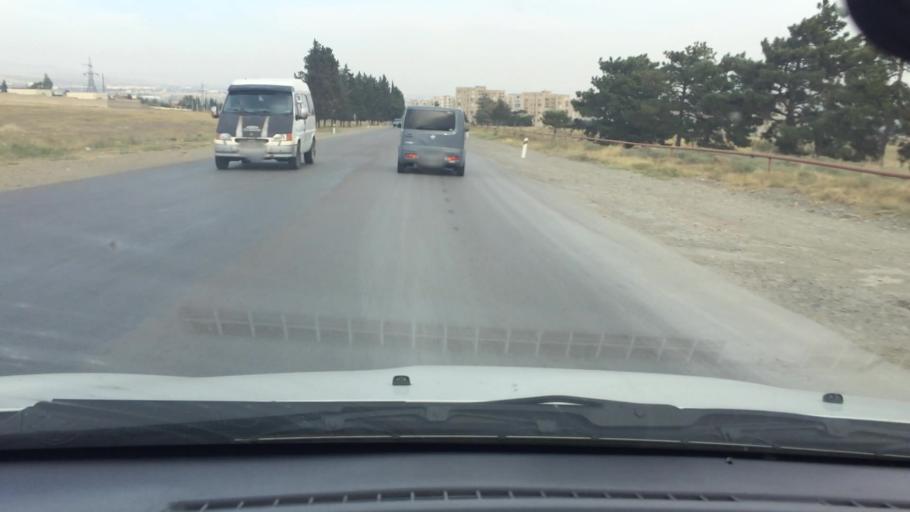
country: GE
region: T'bilisi
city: Tbilisi
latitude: 41.6416
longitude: 44.8861
